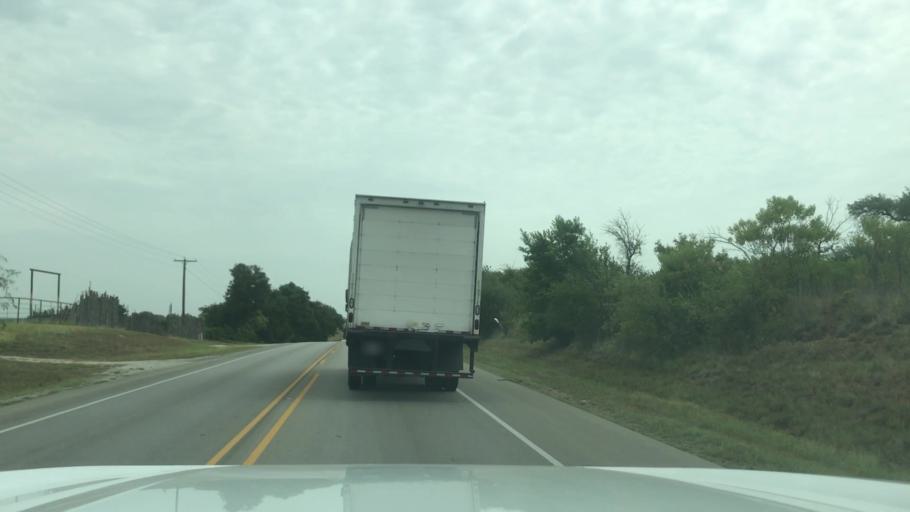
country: US
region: Texas
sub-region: Erath County
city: Dublin
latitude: 32.0895
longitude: -98.4249
